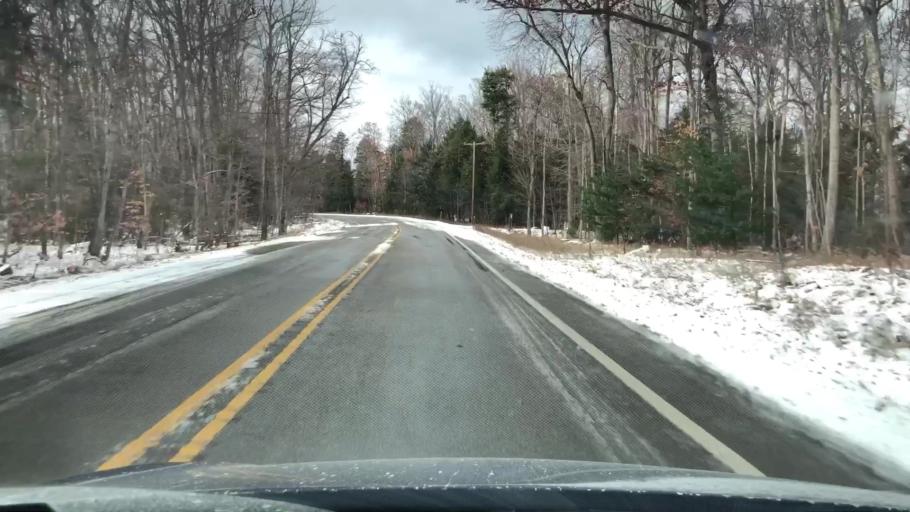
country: US
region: Michigan
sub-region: Antrim County
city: Elk Rapids
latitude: 44.9899
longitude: -85.4888
